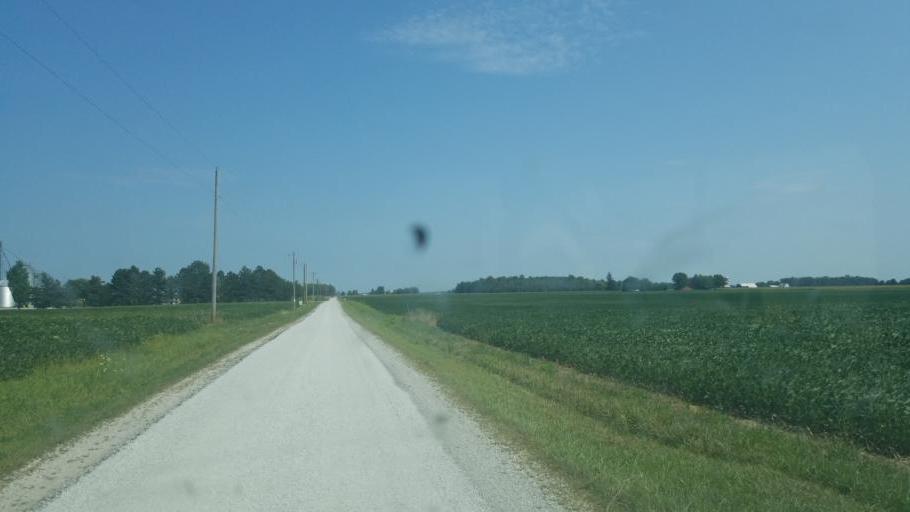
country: US
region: Ohio
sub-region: Crawford County
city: Bucyrus
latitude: 40.9360
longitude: -82.9119
